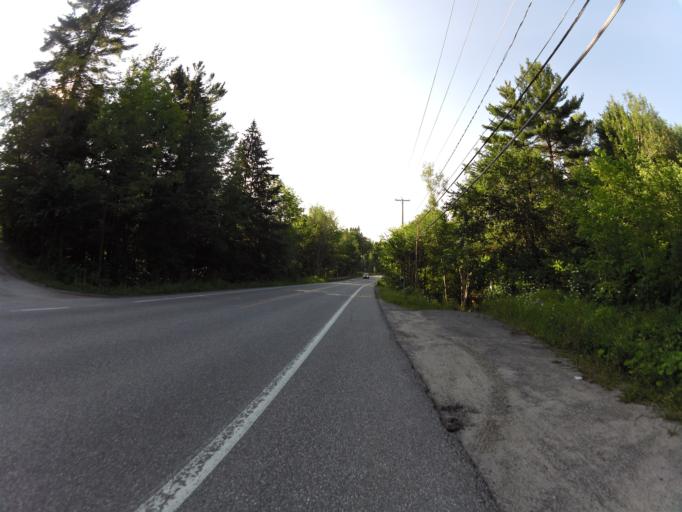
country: CA
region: Quebec
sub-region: Outaouais
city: Gatineau
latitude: 45.5314
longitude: -75.8054
